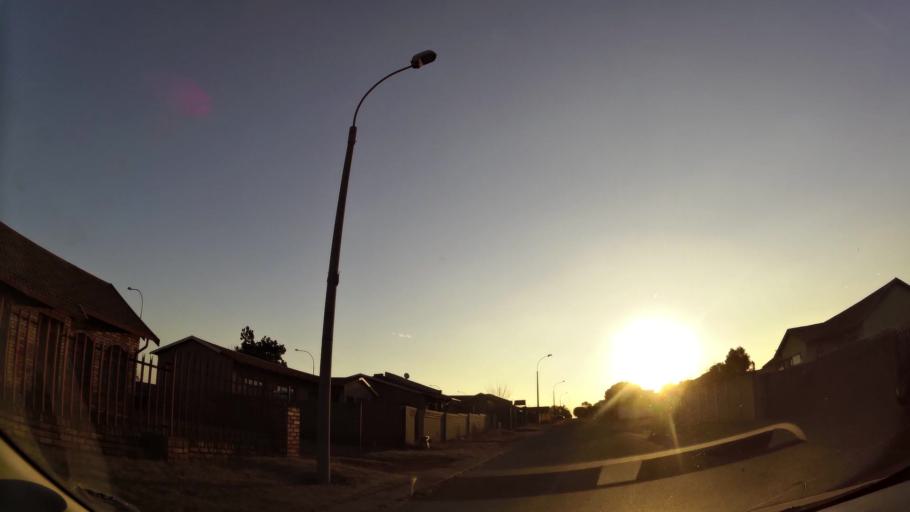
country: ZA
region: Gauteng
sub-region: West Rand District Municipality
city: Randfontein
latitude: -26.2107
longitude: 27.7051
